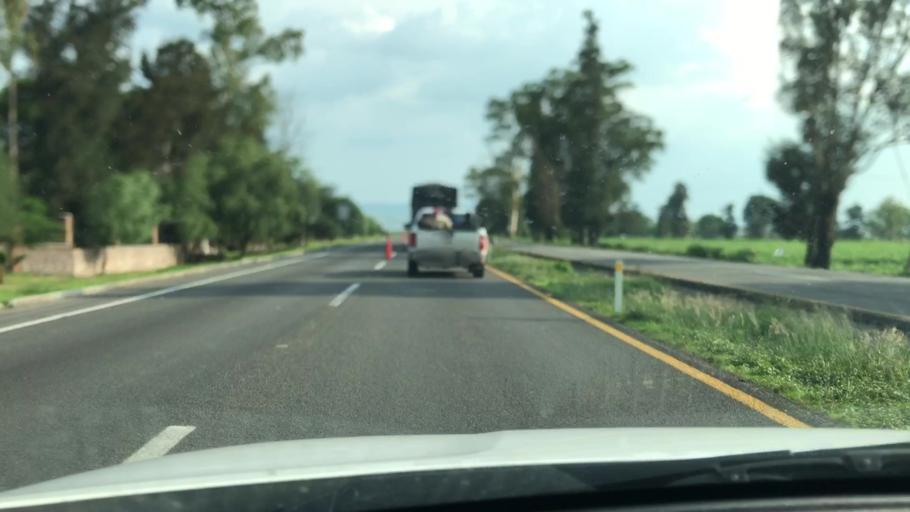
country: MX
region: Guanajuato
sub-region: Irapuato
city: San Ignacio de Rivera (Ojo de Agua)
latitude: 20.5215
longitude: -101.4637
